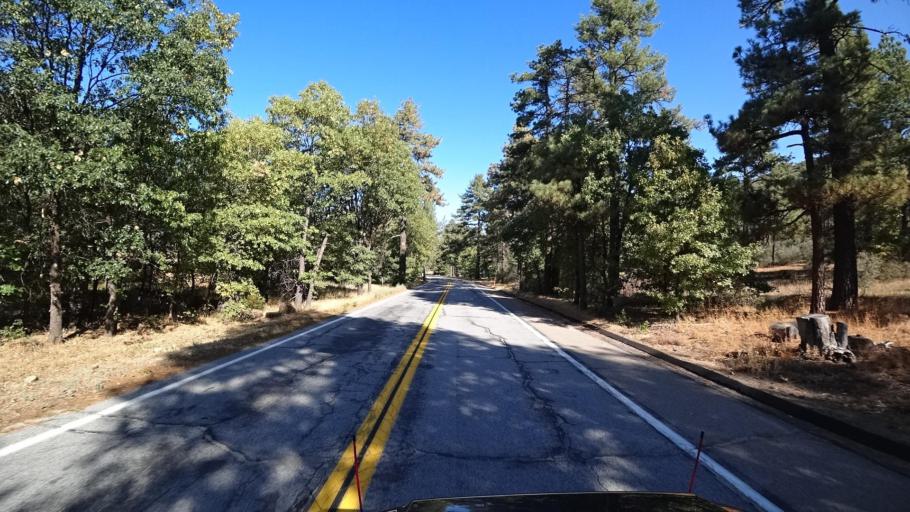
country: US
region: California
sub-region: San Diego County
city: Pine Valley
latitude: 32.8731
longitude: -116.4171
